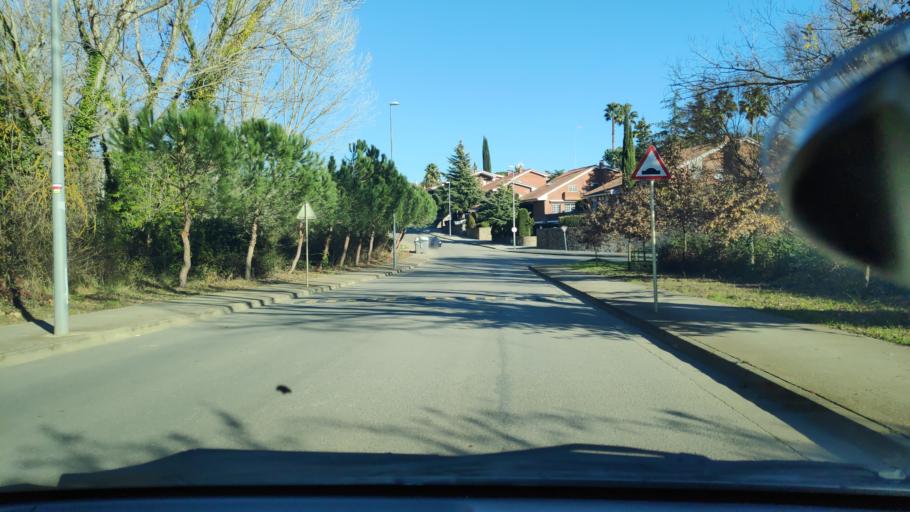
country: ES
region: Catalonia
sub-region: Provincia de Barcelona
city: Sant Quirze del Valles
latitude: 41.5387
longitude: 2.0619
